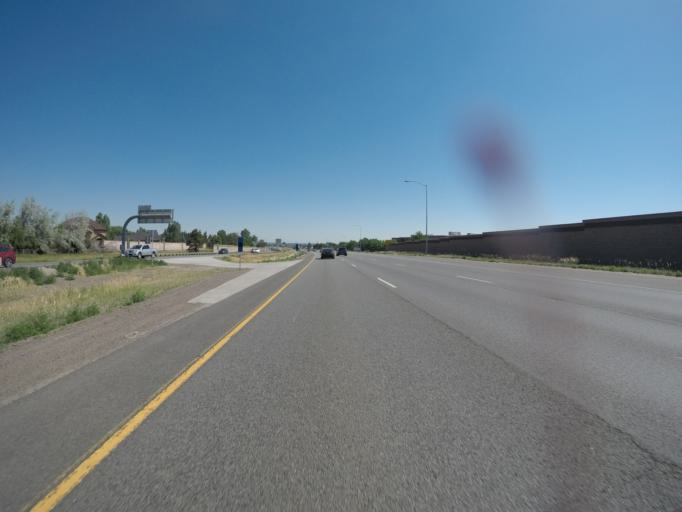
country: US
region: Colorado
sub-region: Jefferson County
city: Applewood
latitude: 39.7552
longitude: -105.1449
